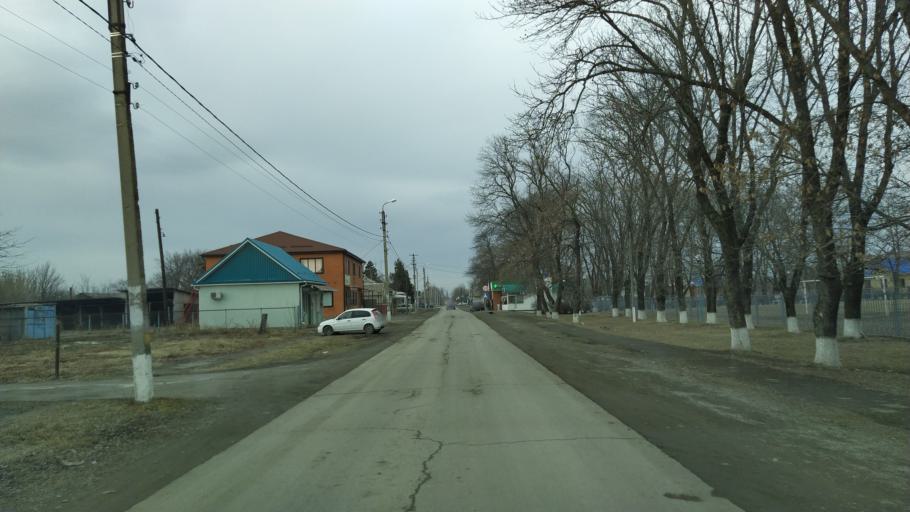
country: RU
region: Krasnodarskiy
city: Udobnaya
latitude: 44.1976
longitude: 41.5525
